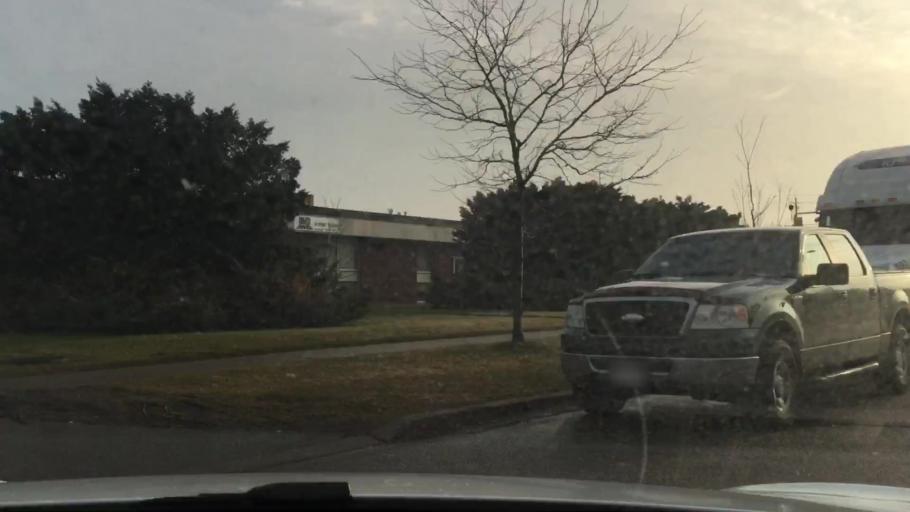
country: CA
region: Ontario
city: Scarborough
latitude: 43.7827
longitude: -79.2378
